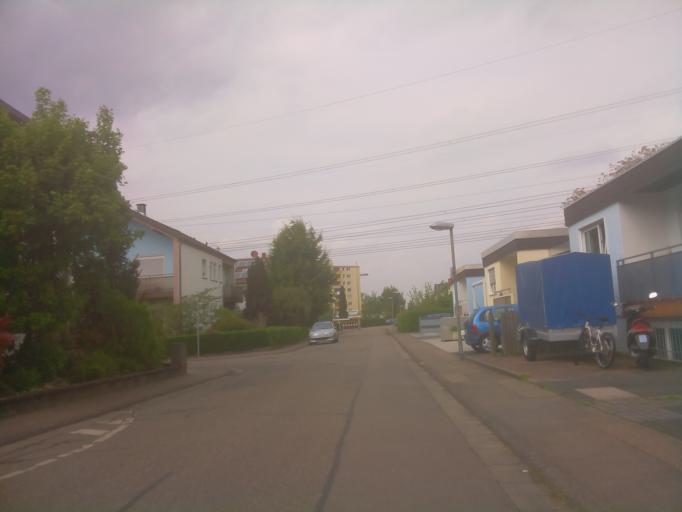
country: DE
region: Baden-Wuerttemberg
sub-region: Karlsruhe Region
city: Sandhausen
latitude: 49.3459
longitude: 8.6680
